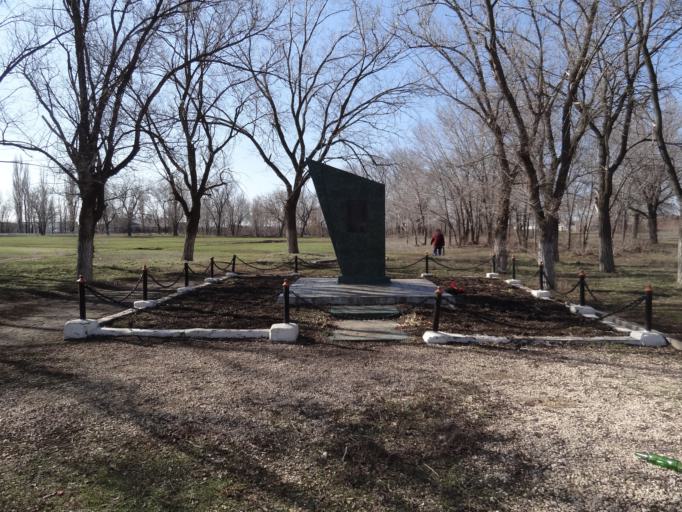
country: RU
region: Saratov
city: Shumeyka
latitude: 51.3899
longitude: 46.2974
